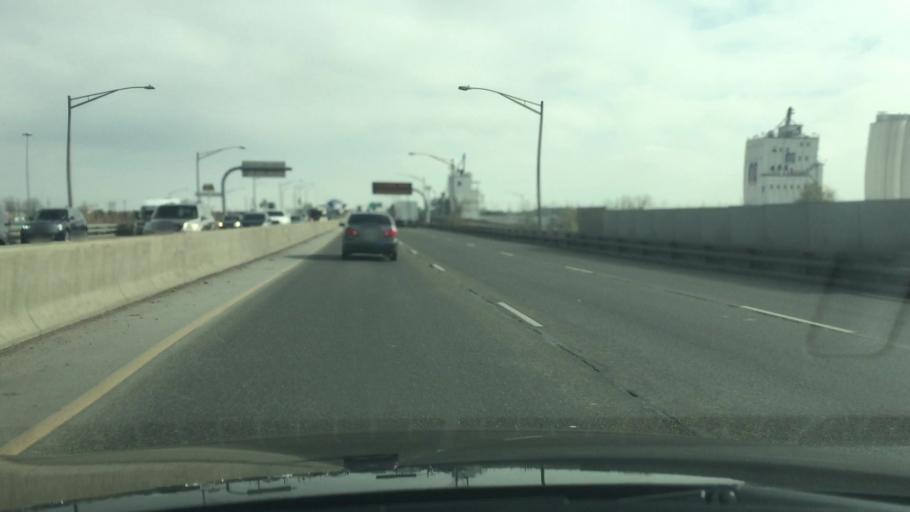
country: US
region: Colorado
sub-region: Adams County
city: Commerce City
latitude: 39.7800
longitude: -104.9501
